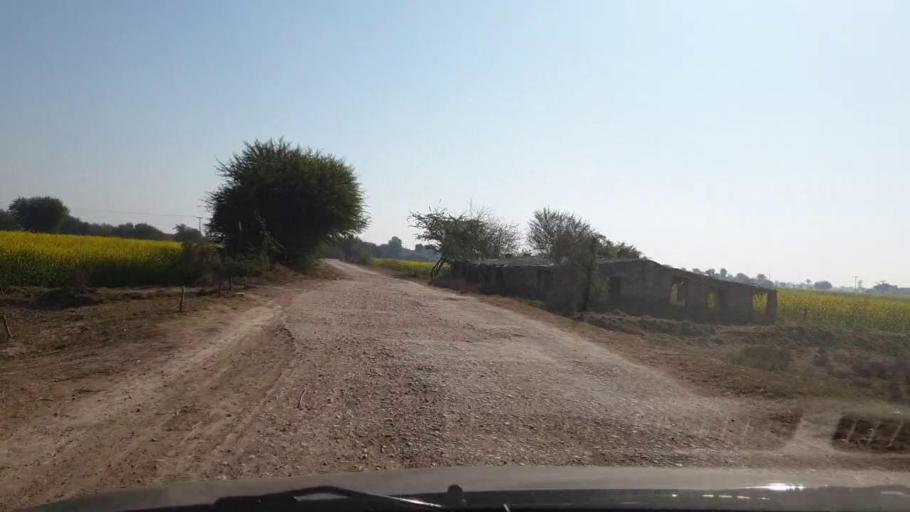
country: PK
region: Sindh
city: Jhol
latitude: 25.9343
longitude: 68.8248
